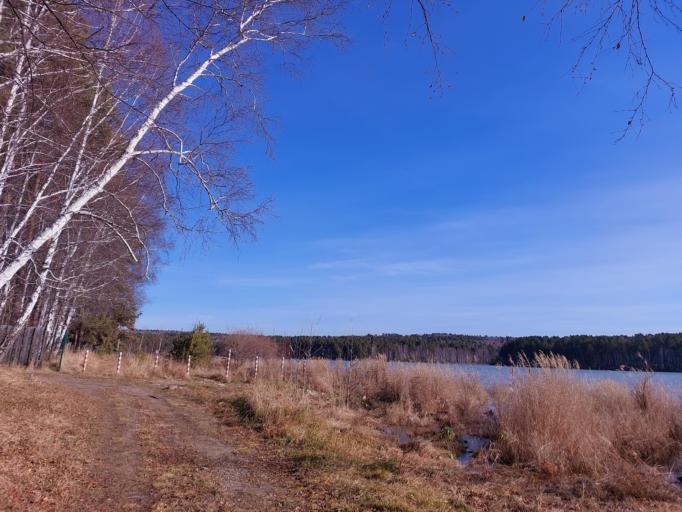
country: RU
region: Irkutsk
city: Pivovarikha
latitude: 52.1839
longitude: 104.4568
